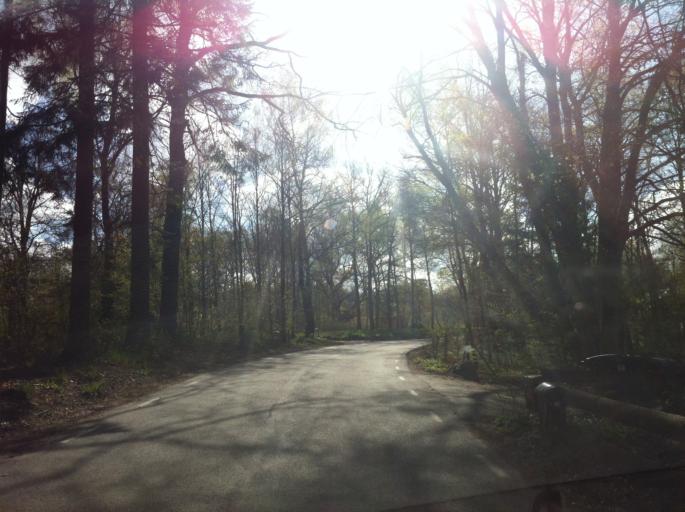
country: SE
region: Skane
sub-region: Hoors Kommun
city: Hoeoer
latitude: 55.9144
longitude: 13.4814
